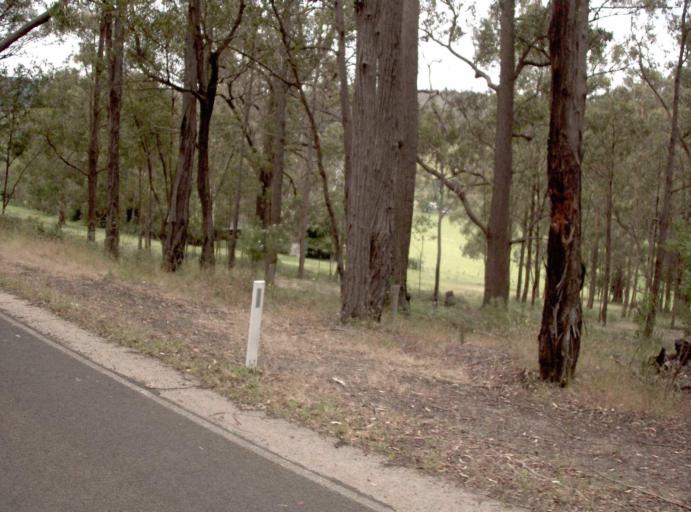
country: AU
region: Victoria
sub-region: Latrobe
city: Traralgon
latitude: -38.4937
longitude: 146.6433
